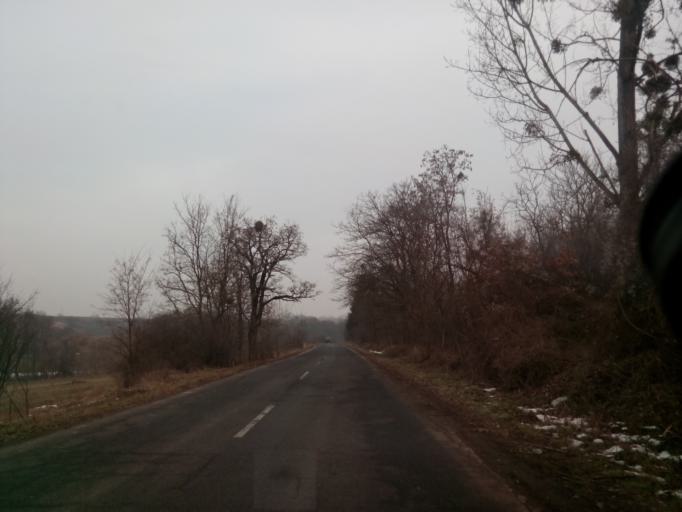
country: HU
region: Borsod-Abauj-Zemplen
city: Gonc
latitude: 48.4979
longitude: 21.3017
